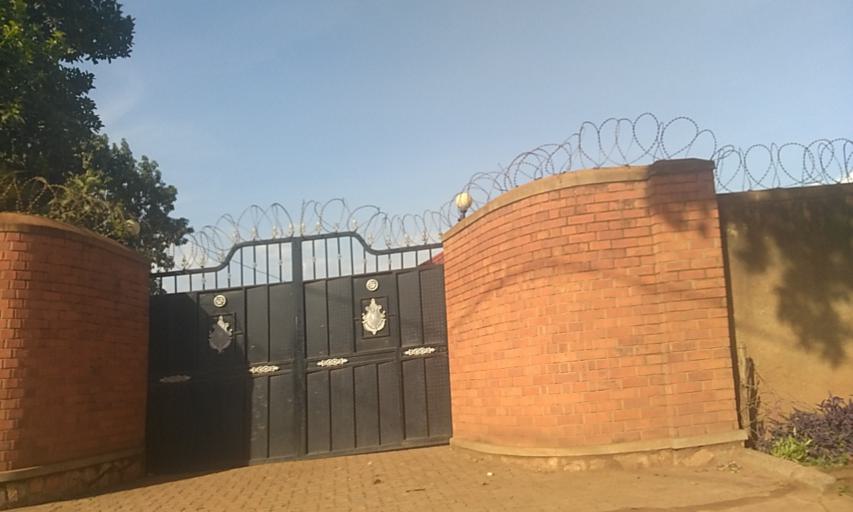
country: UG
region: Central Region
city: Kampala Central Division
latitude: 0.3209
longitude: 32.5457
